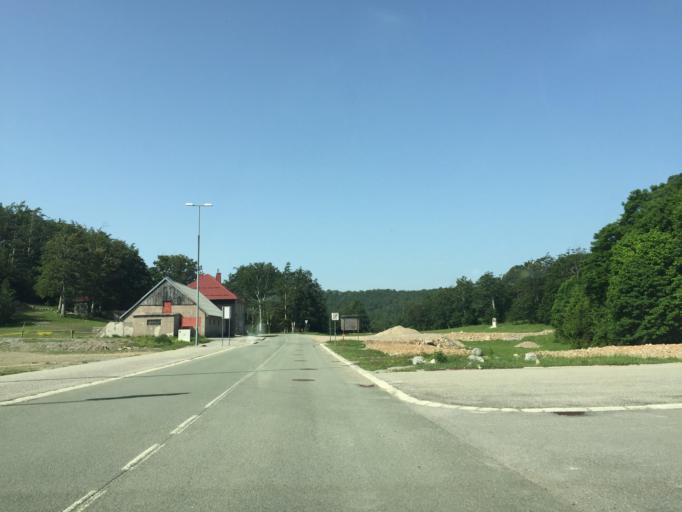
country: HR
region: Primorsko-Goranska
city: Podhum
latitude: 45.4245
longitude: 14.5644
